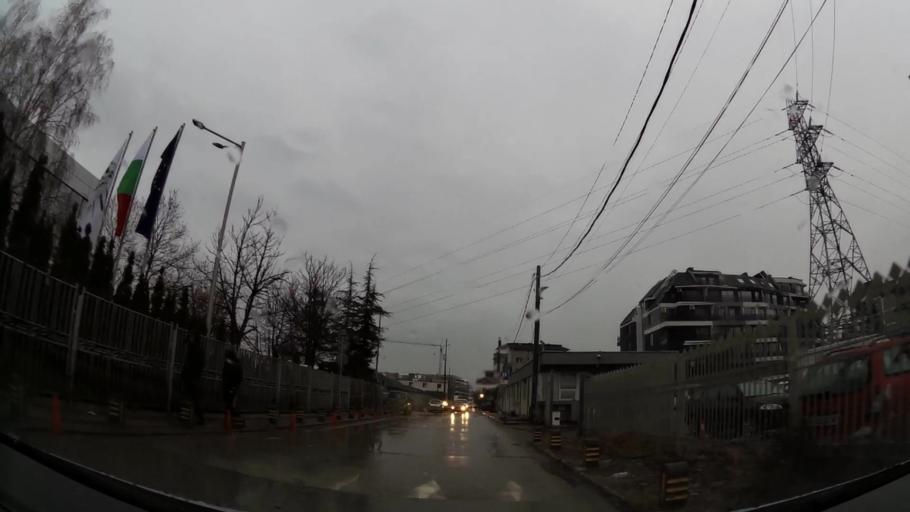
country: BG
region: Sofia-Capital
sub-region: Stolichna Obshtina
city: Sofia
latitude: 42.6548
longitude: 23.3165
